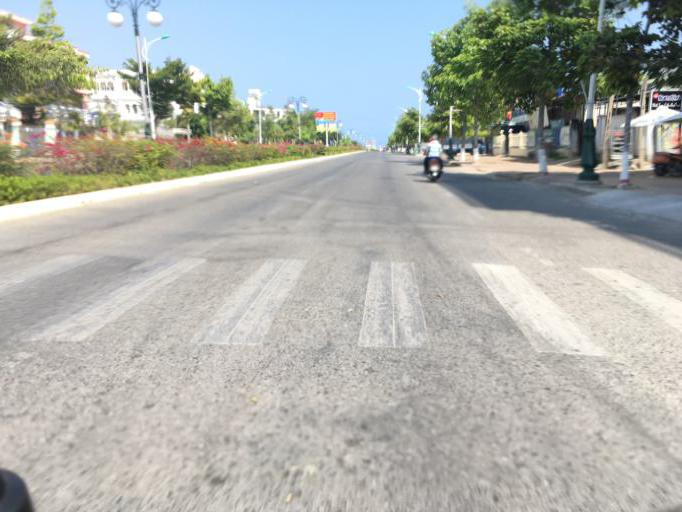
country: VN
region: Ninh Thuan
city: Phan Rang-Thap Cham
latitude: 11.5632
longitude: 109.0178
